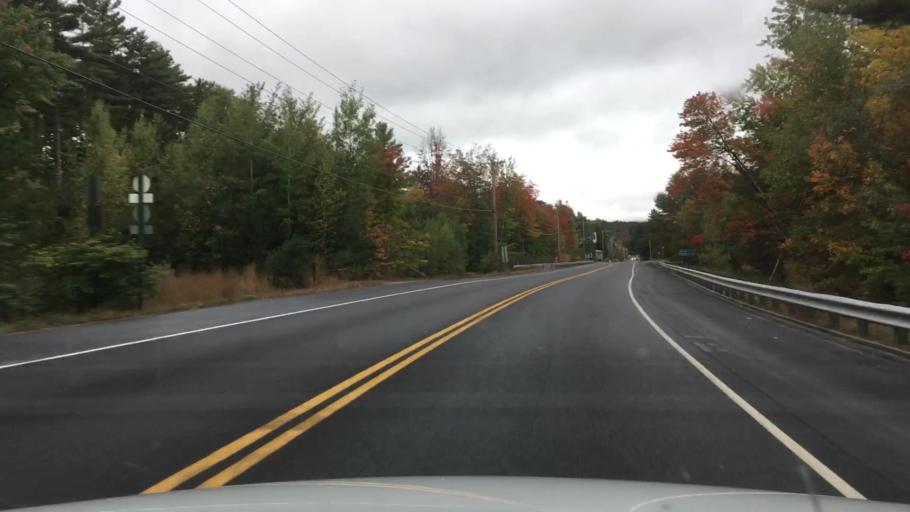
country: US
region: Maine
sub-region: Oxford County
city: Bethel
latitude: 44.4095
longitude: -70.8071
